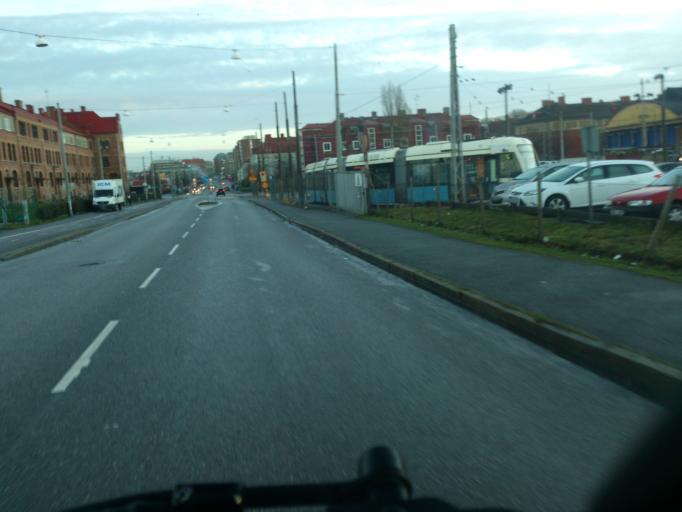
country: SE
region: Vaestra Goetaland
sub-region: Goteborg
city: Majorna
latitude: 57.6883
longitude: 11.9098
